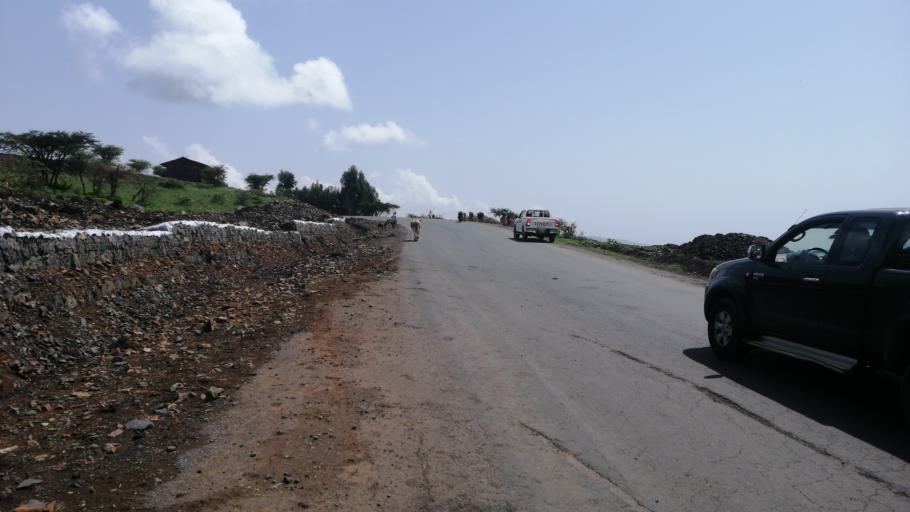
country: ET
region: Oromiya
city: Guder
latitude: 8.9848
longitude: 37.6281
